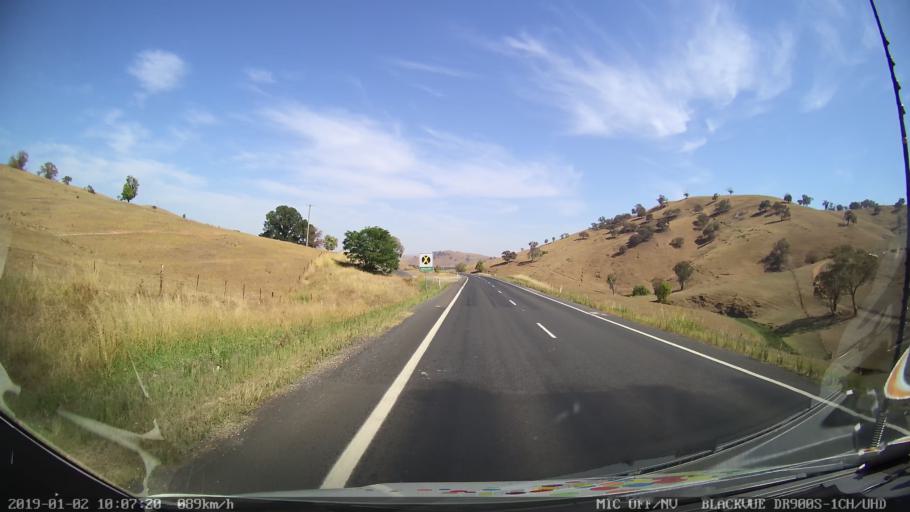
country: AU
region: New South Wales
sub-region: Gundagai
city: Gundagai
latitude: -35.1391
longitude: 148.1140
